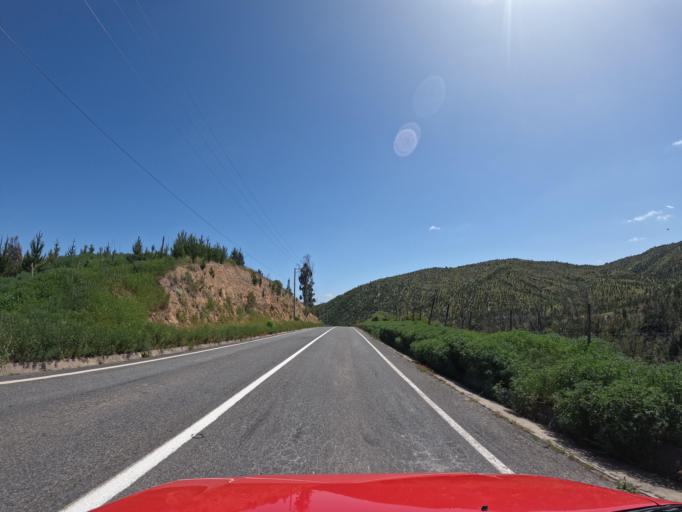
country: CL
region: O'Higgins
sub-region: Provincia de Colchagua
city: Santa Cruz
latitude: -34.6731
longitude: -71.8131
